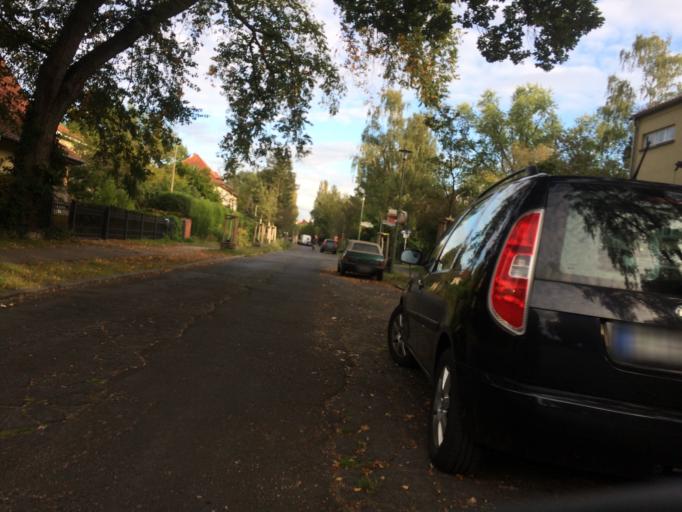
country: DE
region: Berlin
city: Pankow
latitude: 52.5753
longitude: 13.3927
